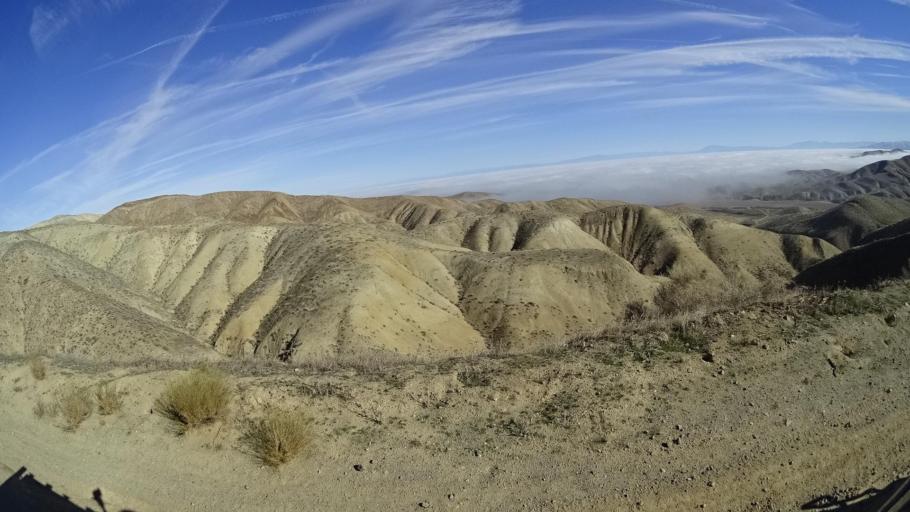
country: US
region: California
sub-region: Kern County
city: Maricopa
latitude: 35.0136
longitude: -119.4684
